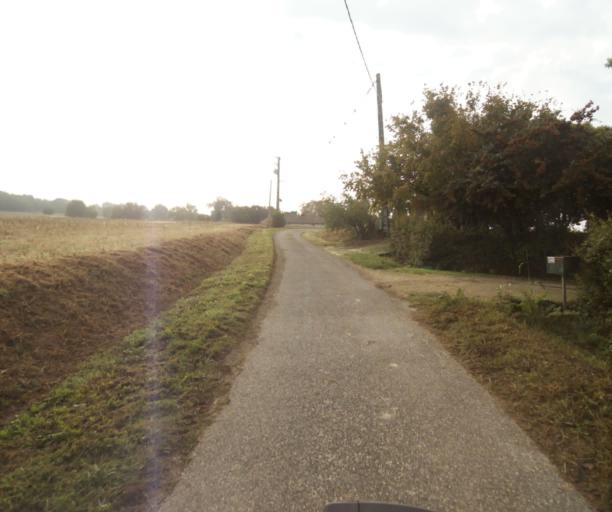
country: FR
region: Midi-Pyrenees
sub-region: Departement du Tarn-et-Garonne
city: Montech
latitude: 43.9481
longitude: 1.2398
